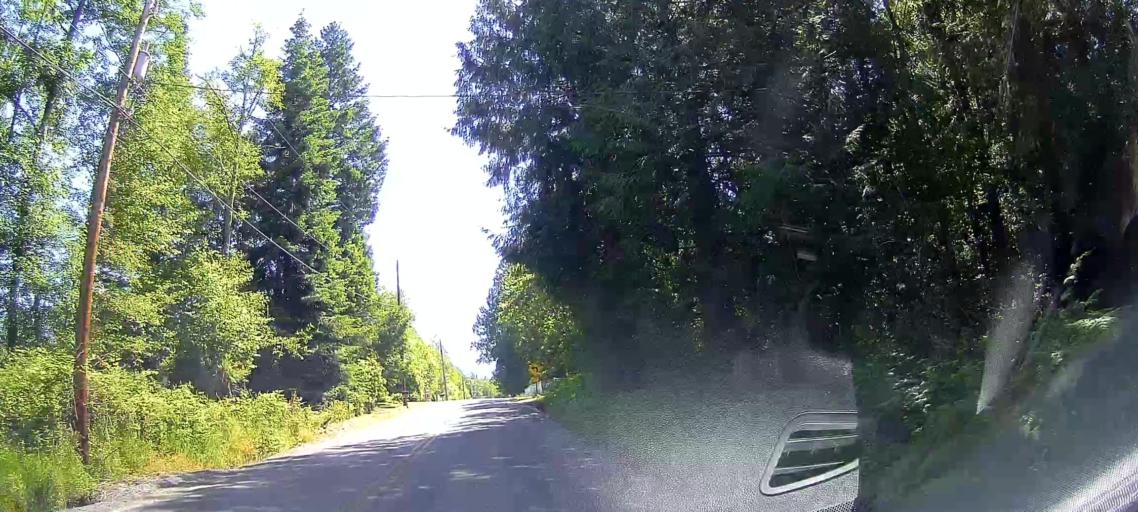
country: US
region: Washington
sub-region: Skagit County
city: Sedro-Woolley
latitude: 48.5546
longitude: -122.2716
